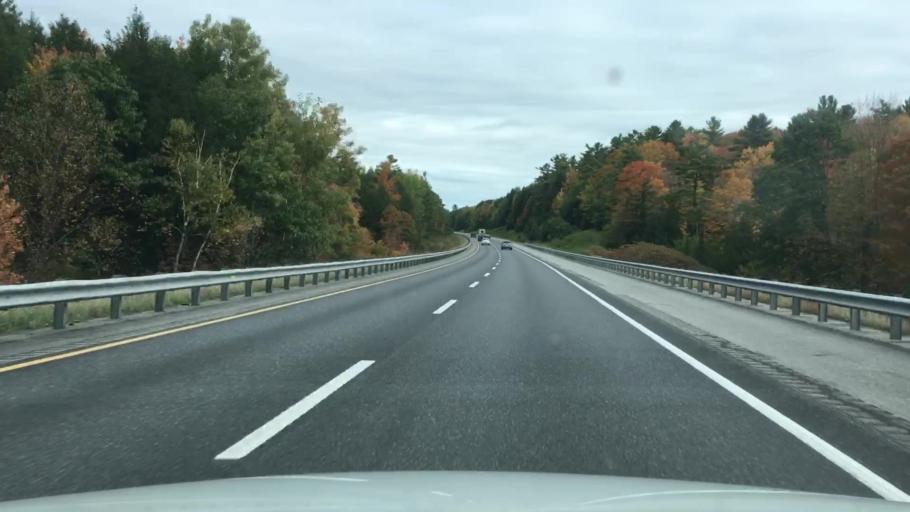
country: US
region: Maine
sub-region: Sagadahoc County
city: Richmond
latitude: 44.0434
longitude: -69.8959
